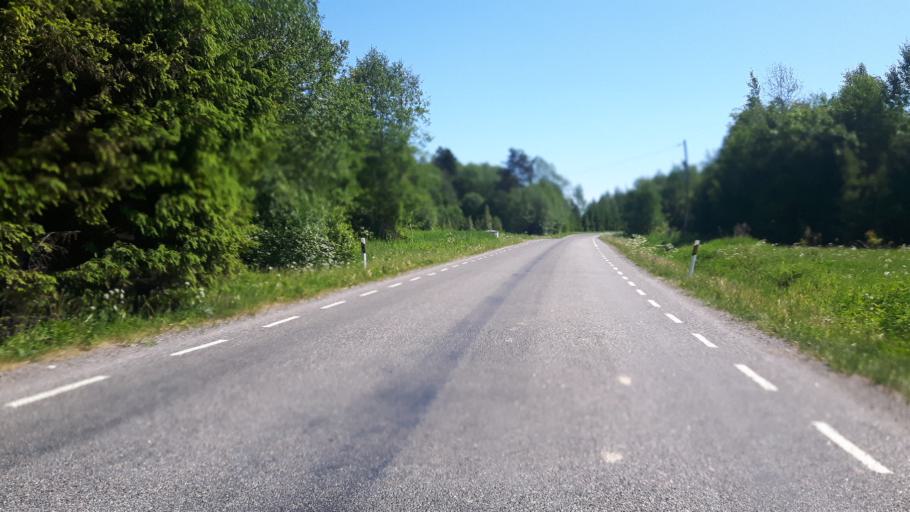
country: EE
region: Raplamaa
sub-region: Kohila vald
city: Kohila
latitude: 59.1801
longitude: 24.7256
